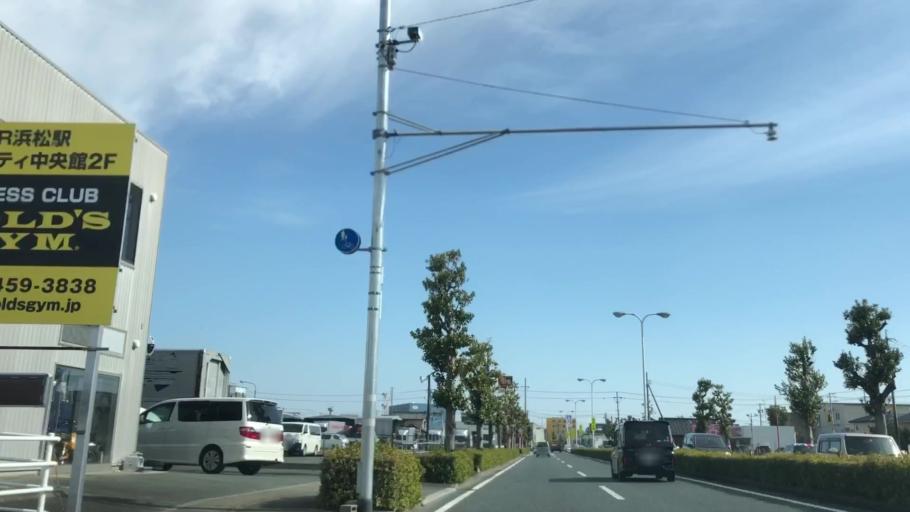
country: JP
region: Shizuoka
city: Hamamatsu
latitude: 34.7604
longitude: 137.6855
